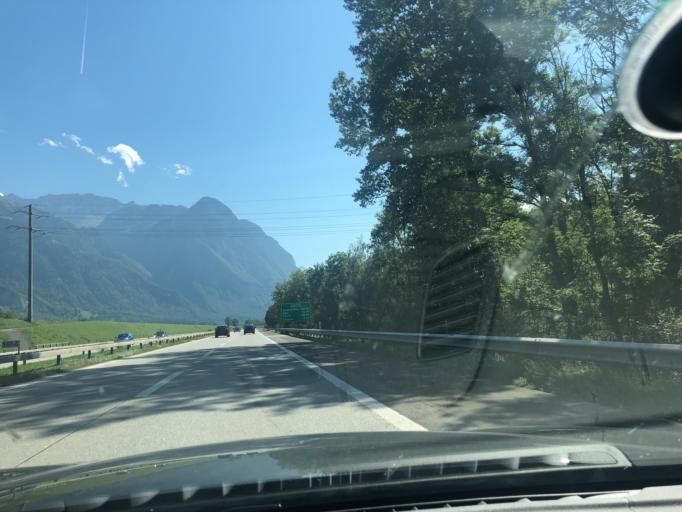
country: LI
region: Triesen
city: Triesen
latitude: 47.1206
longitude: 9.5132
